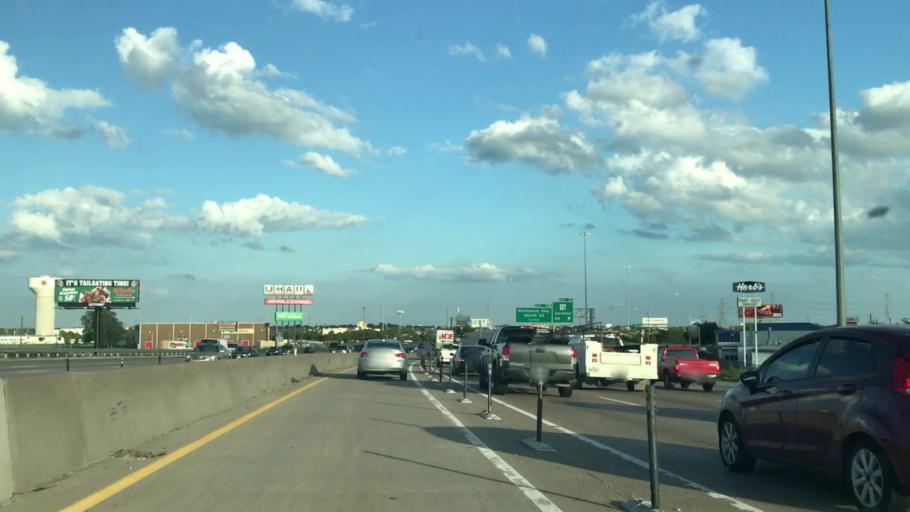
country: US
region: Texas
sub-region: Dallas County
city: Garland
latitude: 32.8703
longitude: -96.6728
